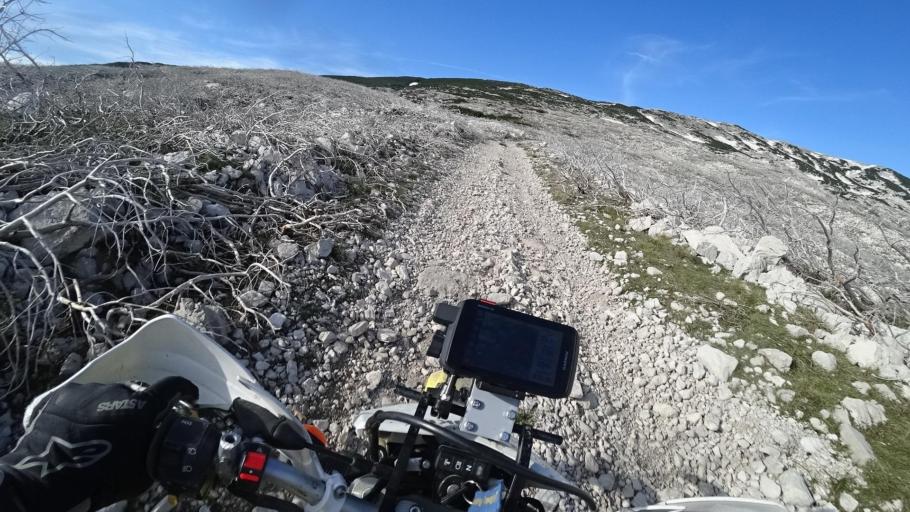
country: BA
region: Federation of Bosnia and Herzegovina
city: Kocerin
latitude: 43.5891
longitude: 17.5375
